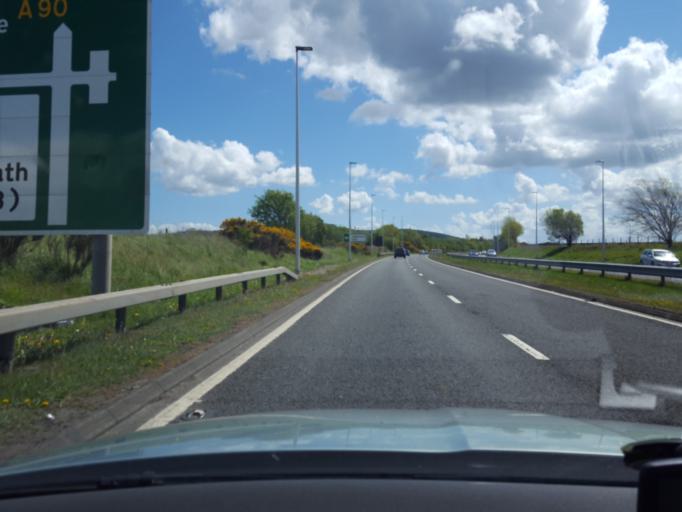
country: GB
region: Scotland
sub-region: Angus
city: Forfar
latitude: 56.6213
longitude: -2.9069
